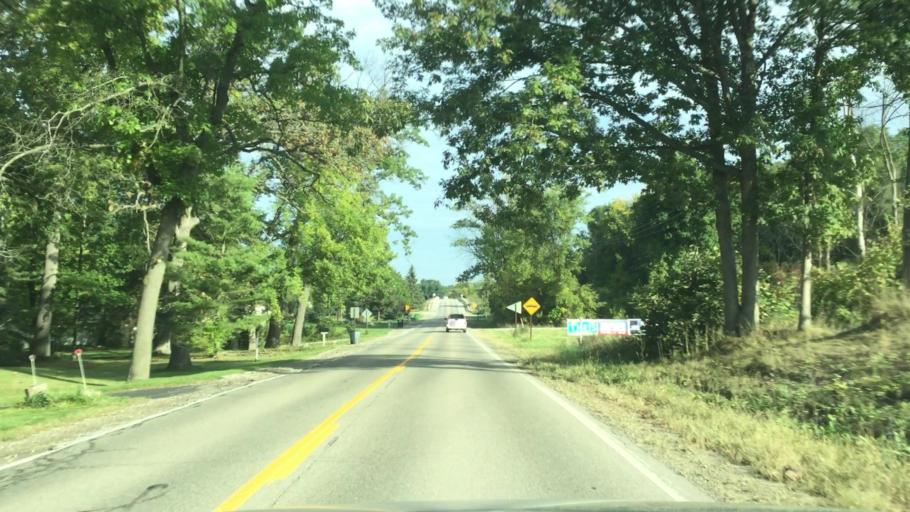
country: US
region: Michigan
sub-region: Livingston County
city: Howell
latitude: 42.5781
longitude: -83.8954
